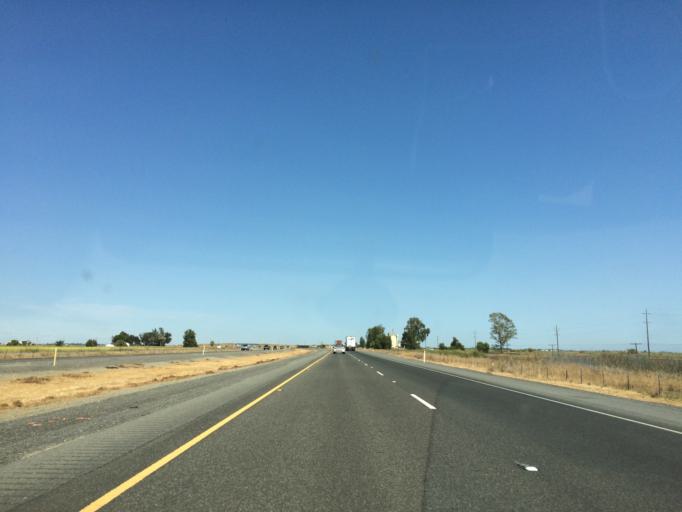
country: US
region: California
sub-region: Glenn County
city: Willows
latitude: 39.4537
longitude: -122.1934
